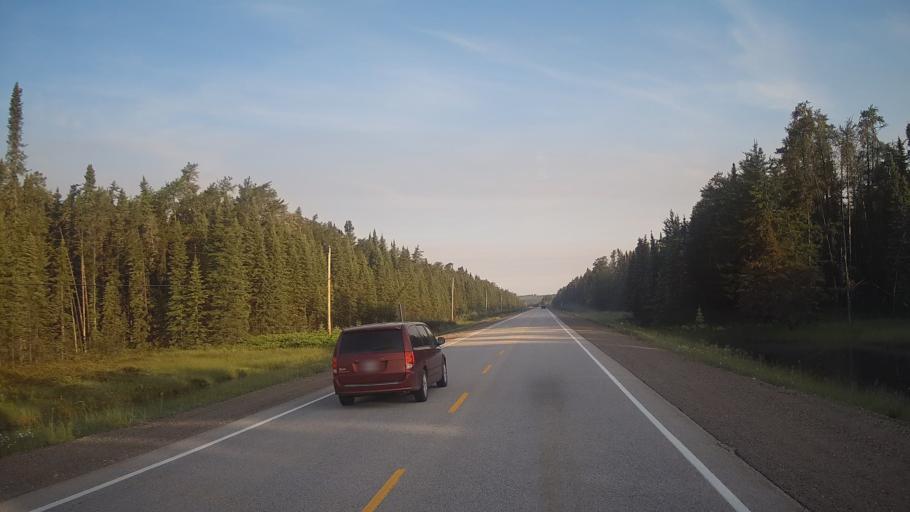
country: CA
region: Ontario
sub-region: Rainy River District
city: Atikokan
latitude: 49.2444
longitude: -91.0914
